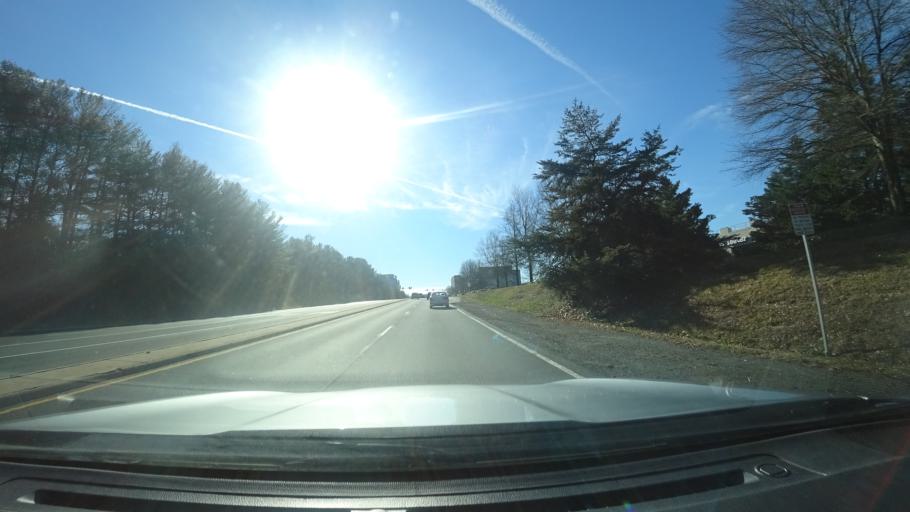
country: US
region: Virginia
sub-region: Fairfax County
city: Reston
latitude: 38.9665
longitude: -77.3539
